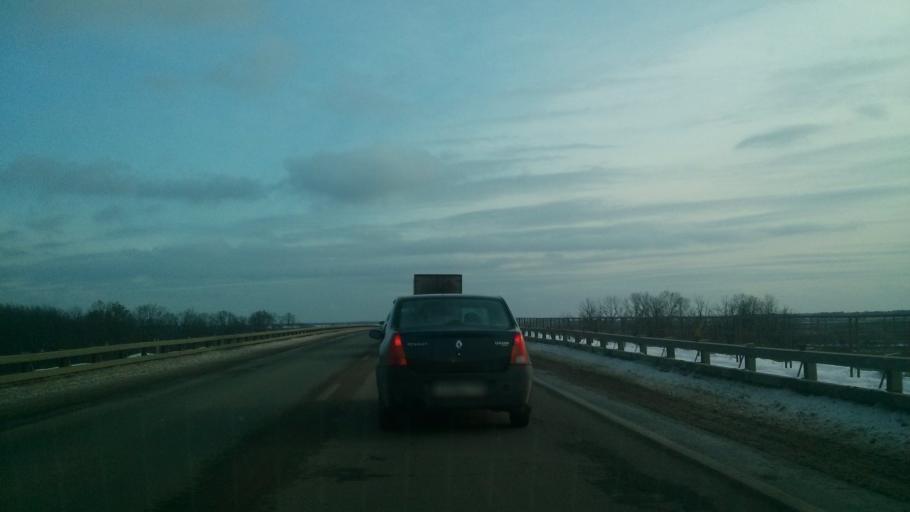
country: RU
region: Vladimir
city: Murom
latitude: 55.6013
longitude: 42.0992
